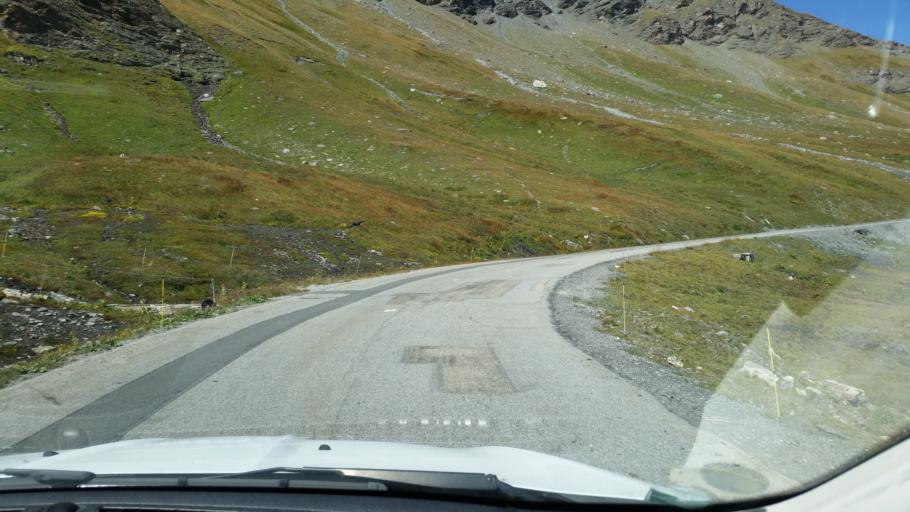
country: FR
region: Rhone-Alpes
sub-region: Departement de la Savoie
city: Val-d'Isere
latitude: 45.4092
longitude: 7.0276
